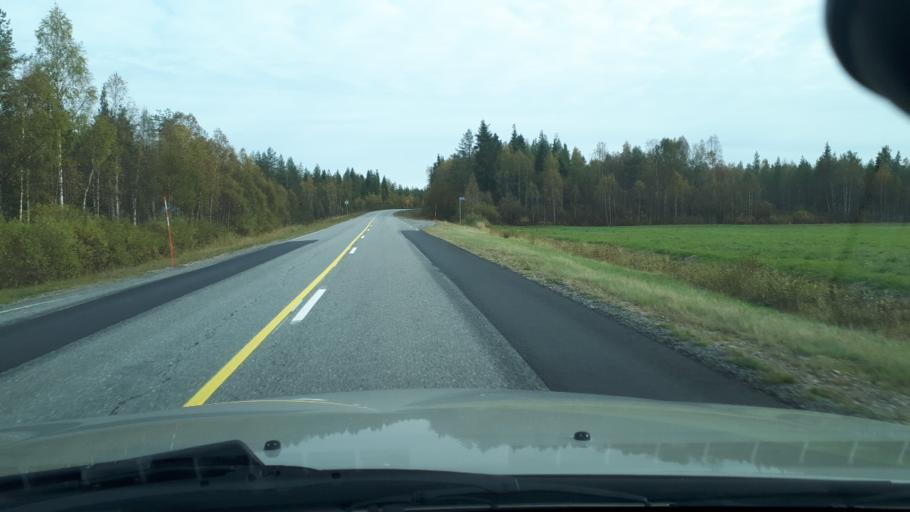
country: FI
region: Lapland
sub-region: Rovaniemi
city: Ranua
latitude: 66.0013
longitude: 26.2440
